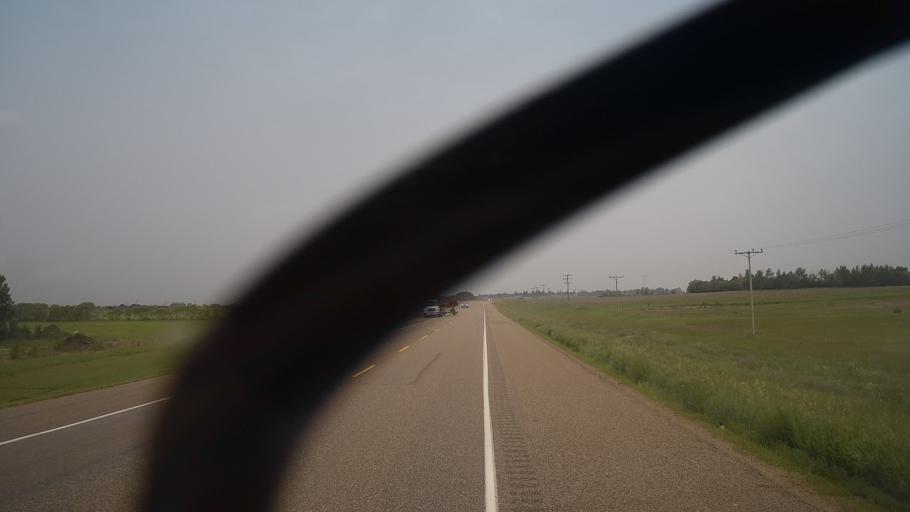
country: CA
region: Saskatchewan
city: Biggar
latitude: 52.0563
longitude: -107.9398
